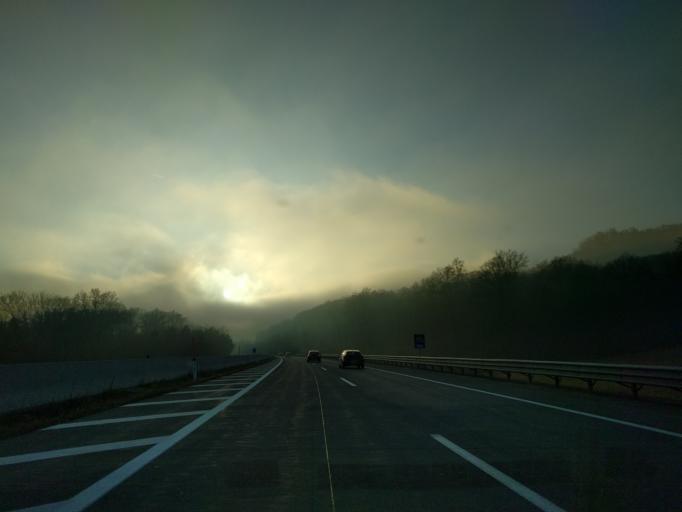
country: AT
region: Lower Austria
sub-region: Politischer Bezirk Wien-Umgebung
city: Purkersdorf
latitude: 48.1911
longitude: 16.1972
